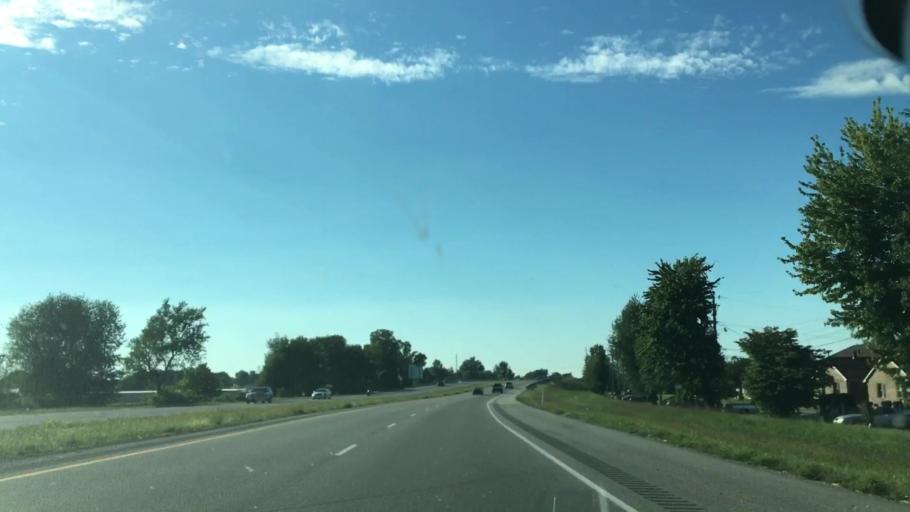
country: US
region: Kentucky
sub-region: Daviess County
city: Owensboro
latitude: 37.7318
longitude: -87.1326
